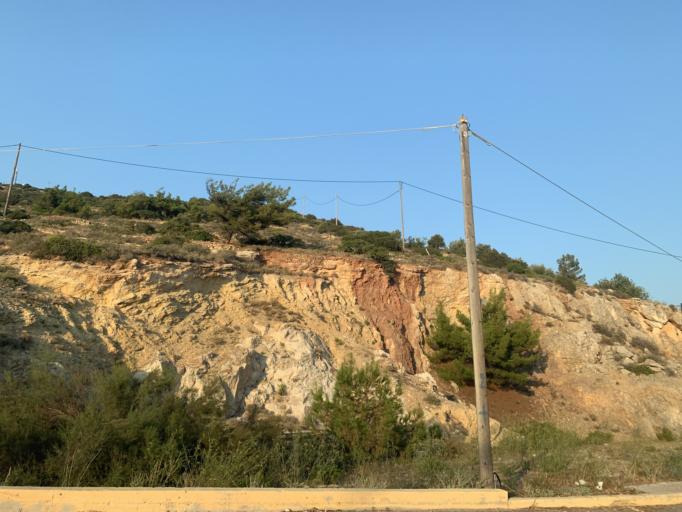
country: GR
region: North Aegean
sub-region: Chios
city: Thymiana
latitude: 38.2897
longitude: 25.9306
